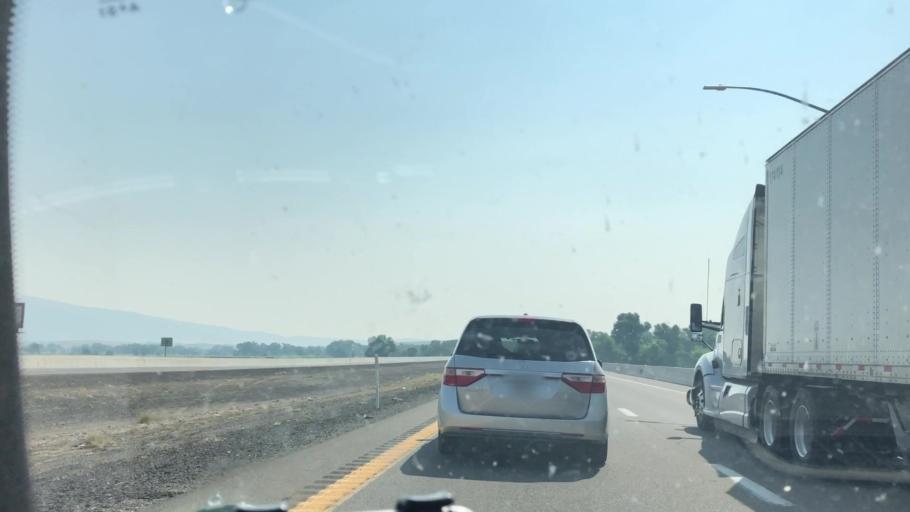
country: US
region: Nevada
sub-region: Lyon County
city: Fernley
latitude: 39.6168
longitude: -119.3047
